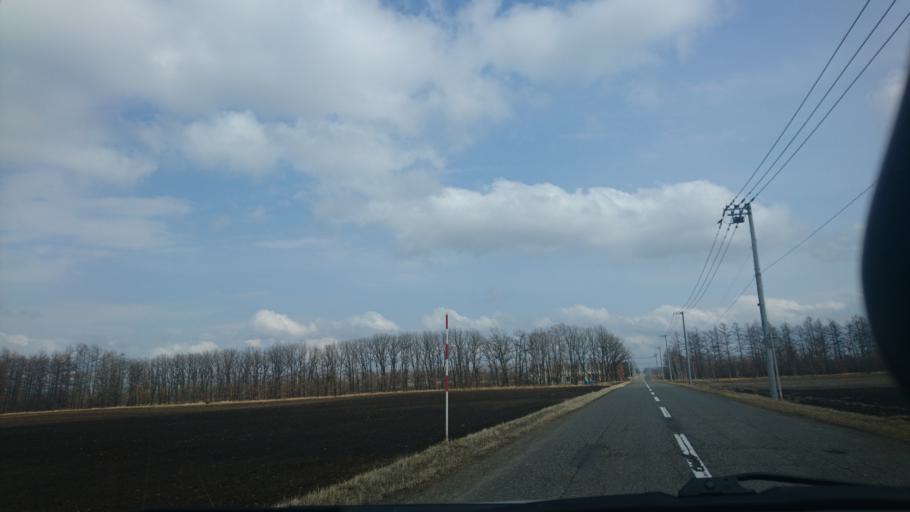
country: JP
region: Hokkaido
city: Otofuke
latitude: 43.2076
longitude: 143.2687
